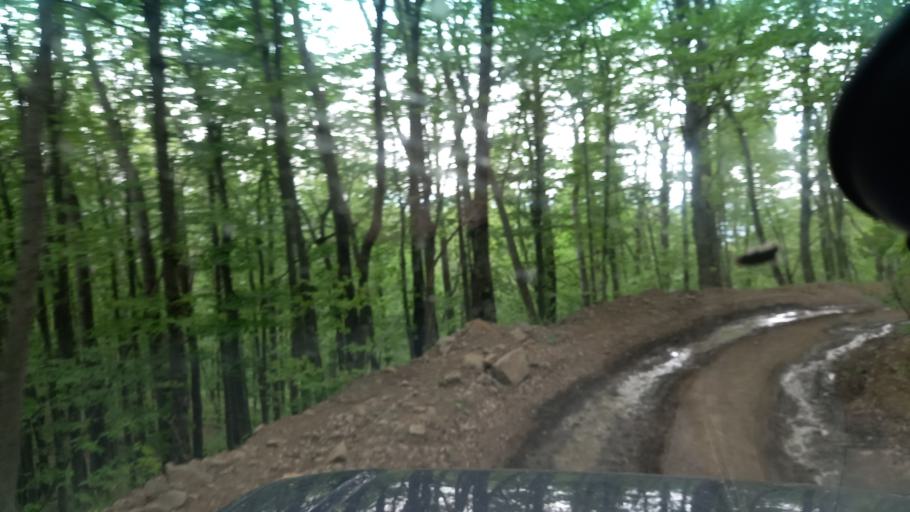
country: RU
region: Krasnodarskiy
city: Tuapse
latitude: 44.2519
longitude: 39.2826
